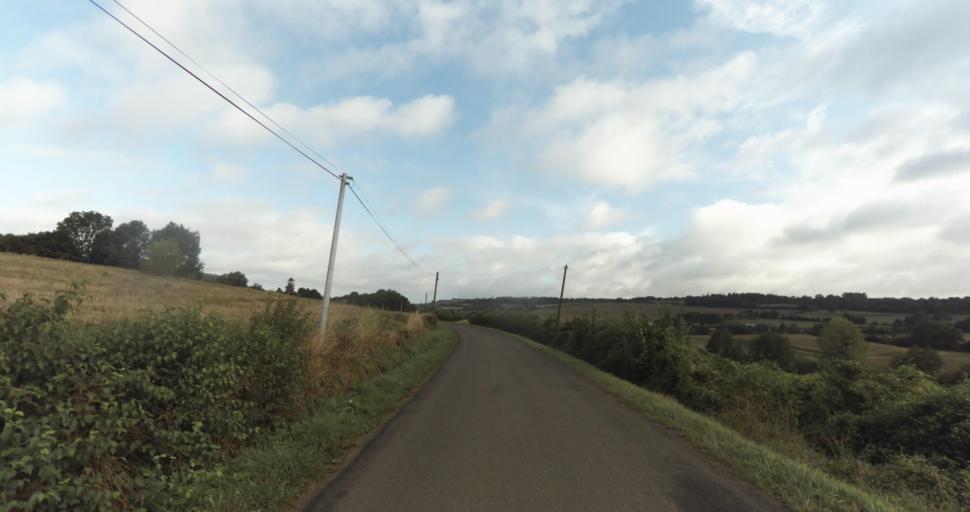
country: FR
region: Lower Normandy
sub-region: Departement de l'Orne
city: Gace
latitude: 48.8806
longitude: 0.2769
